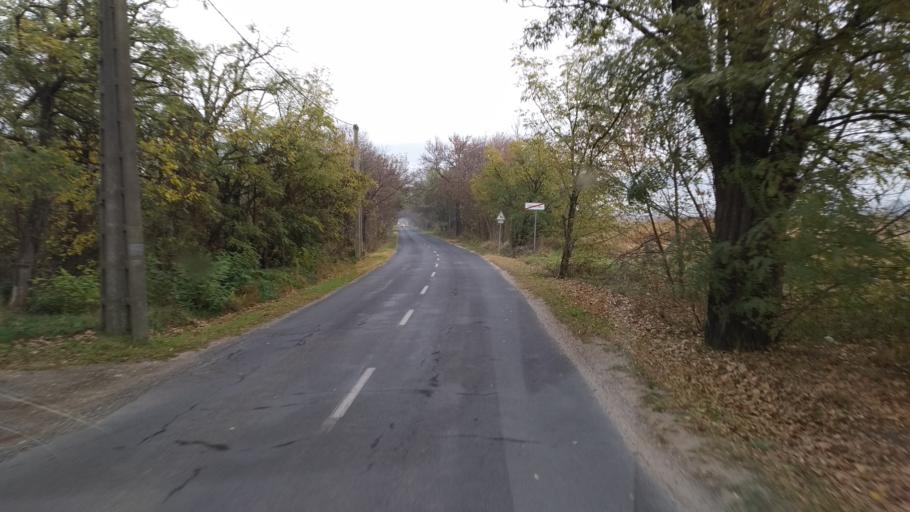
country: HU
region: Pest
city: Tahitotfalu
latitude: 47.7612
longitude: 19.0852
